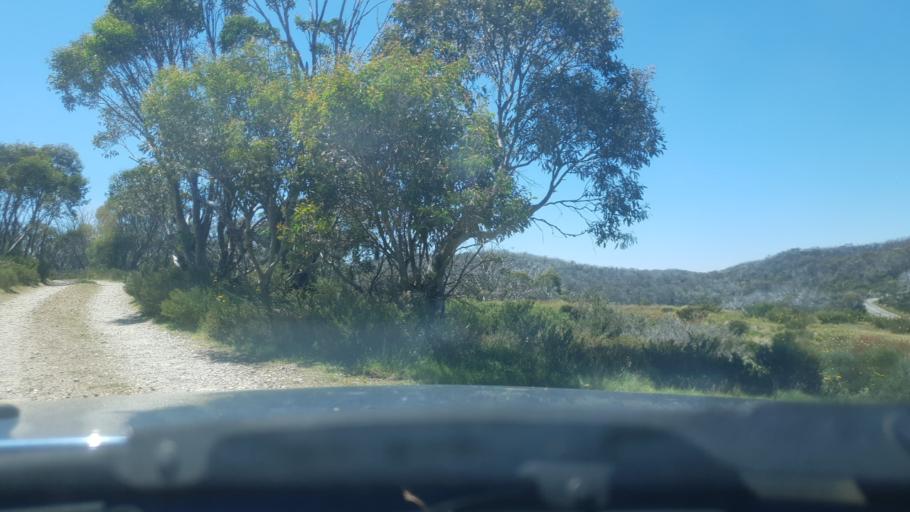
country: AU
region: Victoria
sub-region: Alpine
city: Mount Beauty
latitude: -36.9290
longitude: 147.3018
